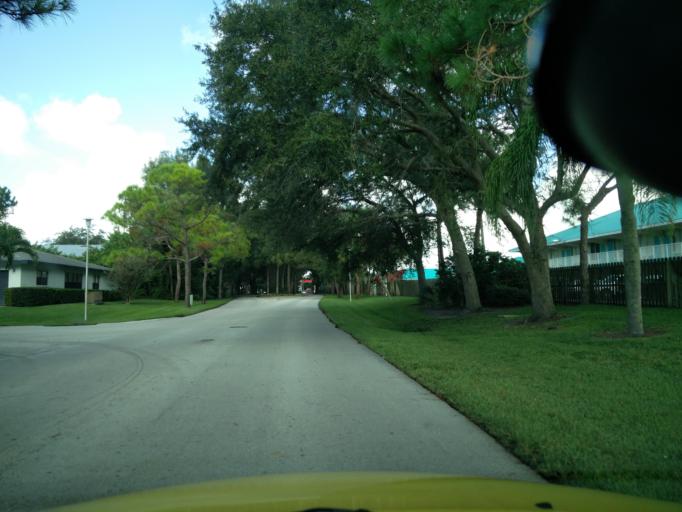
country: US
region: Florida
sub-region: Saint Lucie County
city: Fort Pierce South
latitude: 27.4065
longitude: -80.3236
